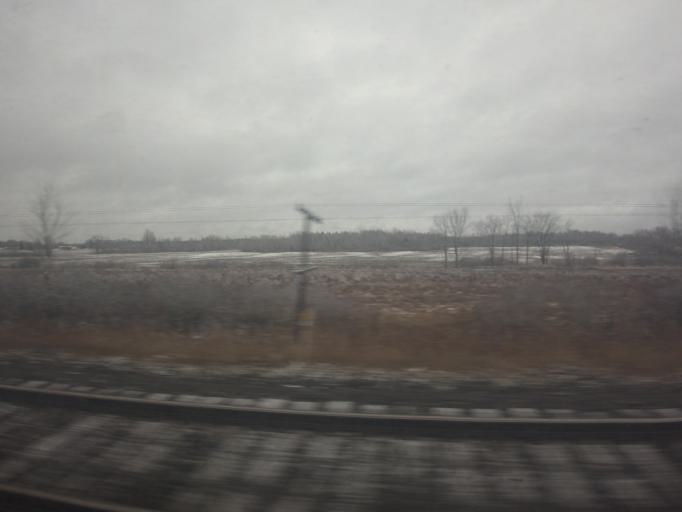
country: US
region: New York
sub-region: Jefferson County
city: Alexandria Bay
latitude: 44.3982
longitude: -76.0267
